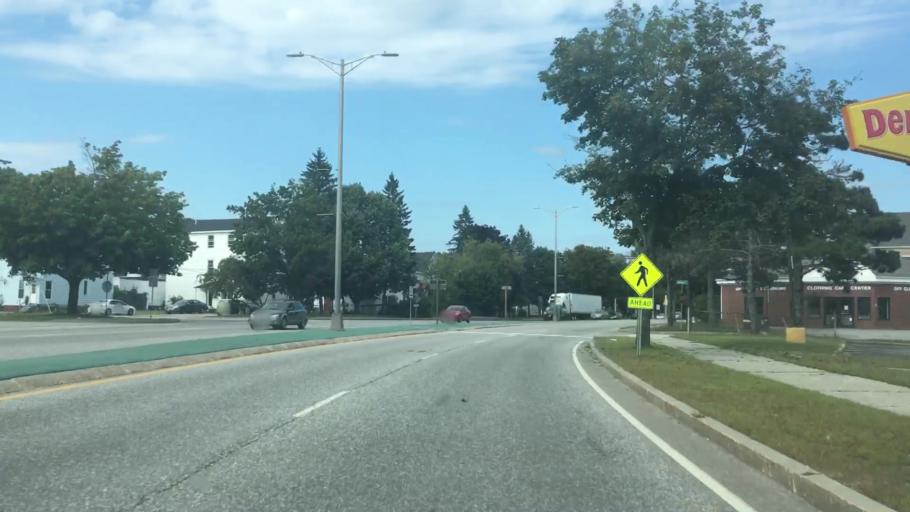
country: US
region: Maine
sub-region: Androscoggin County
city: Auburn
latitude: 44.0984
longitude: -70.2310
